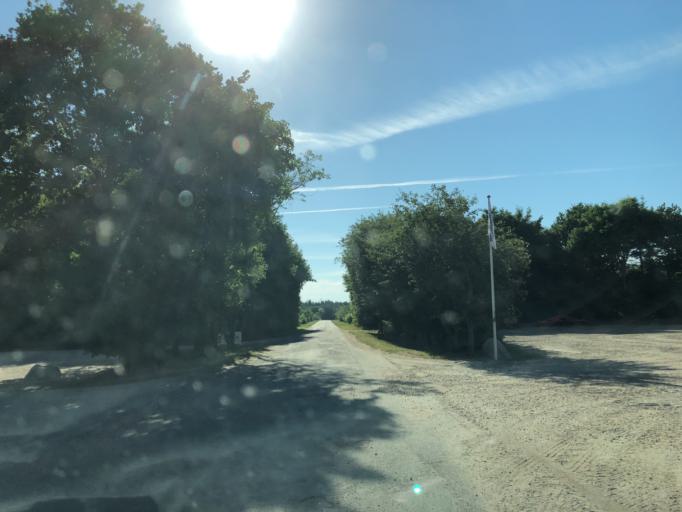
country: DK
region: Central Jutland
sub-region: Holstebro Kommune
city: Ulfborg
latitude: 56.3206
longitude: 8.3876
